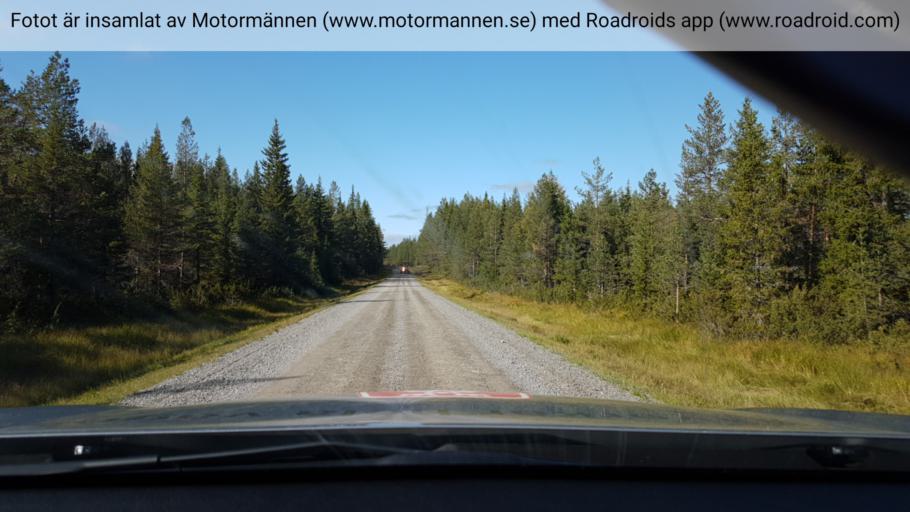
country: SE
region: Norrbotten
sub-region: Arvidsjaurs Kommun
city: Arvidsjaur
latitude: 65.2101
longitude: 19.1360
